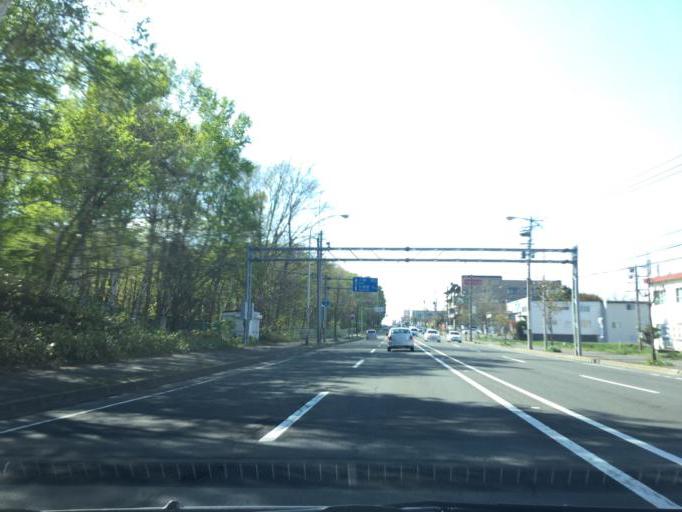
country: JP
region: Hokkaido
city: Sapporo
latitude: 43.0091
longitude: 141.4247
